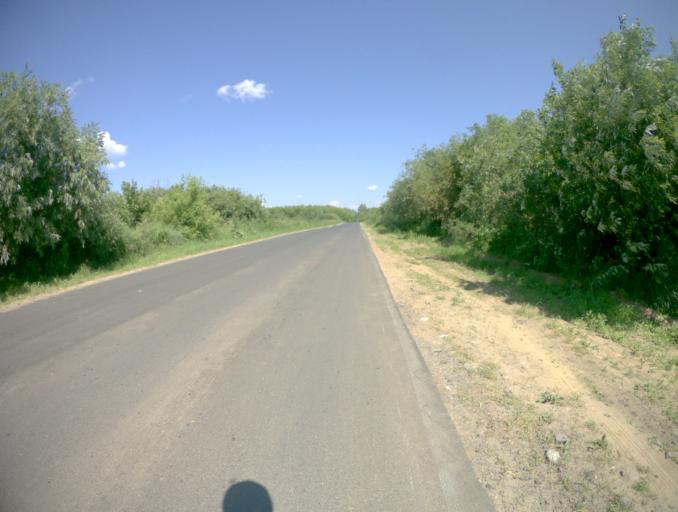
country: RU
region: Vladimir
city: Vyazniki
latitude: 56.2574
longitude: 42.1741
